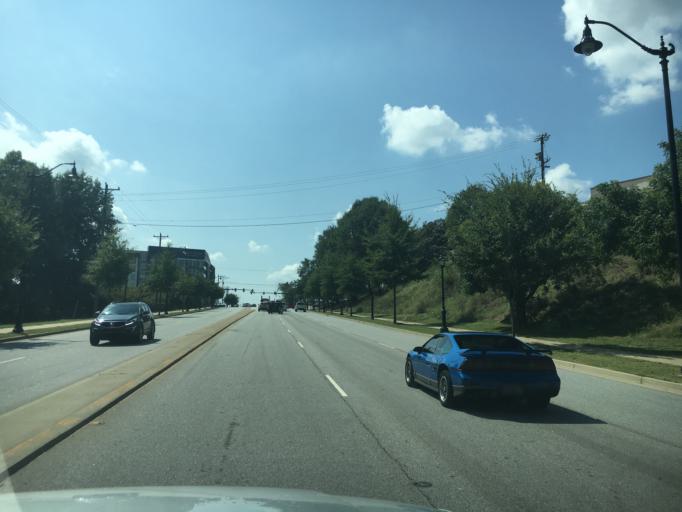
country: US
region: South Carolina
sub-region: Greenville County
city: Greenville
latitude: 34.8421
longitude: -82.3989
